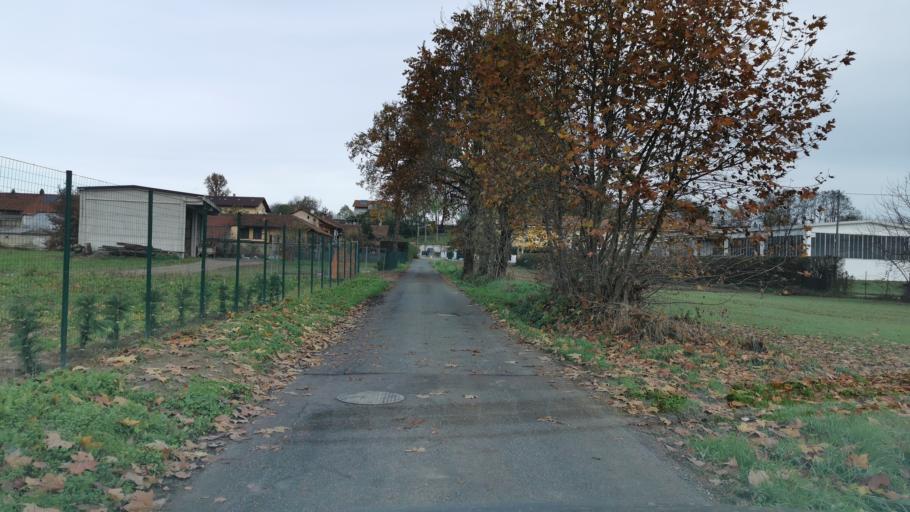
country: IT
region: Piedmont
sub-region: Provincia di Torino
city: San Francesco al Campo
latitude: 45.2155
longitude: 7.6785
